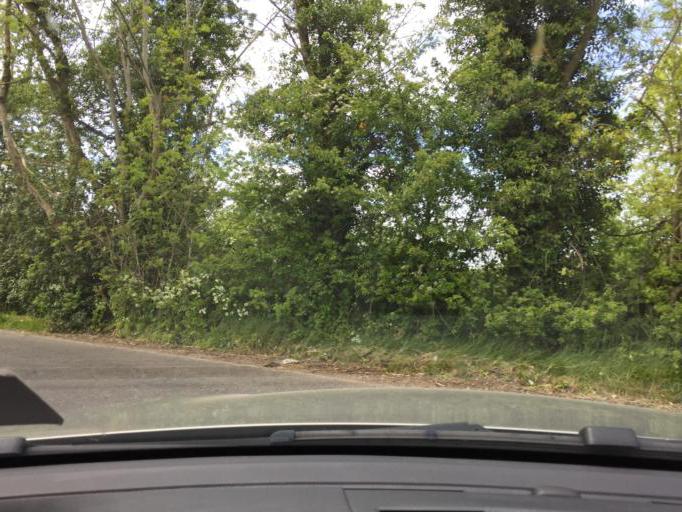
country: GB
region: Northern Ireland
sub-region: Craigavon District
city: Craigavon
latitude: 54.4567
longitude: -6.4051
